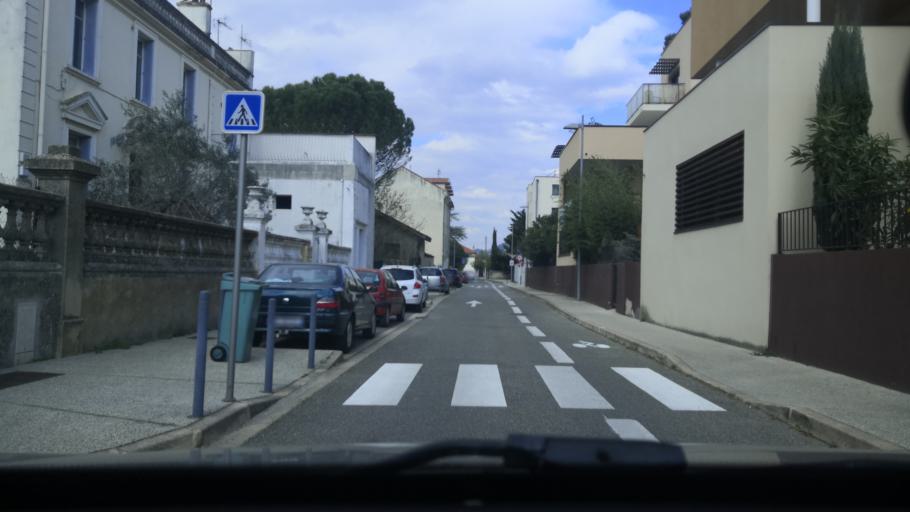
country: FR
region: Rhone-Alpes
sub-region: Departement de la Drome
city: Montelimar
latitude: 44.5641
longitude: 4.7499
